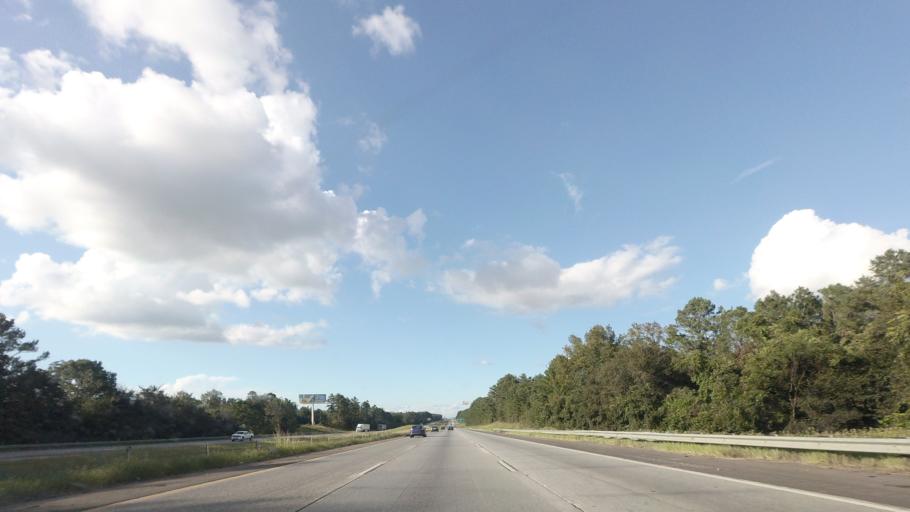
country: US
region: Georgia
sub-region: Houston County
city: Centerville
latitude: 32.5613
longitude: -83.7440
